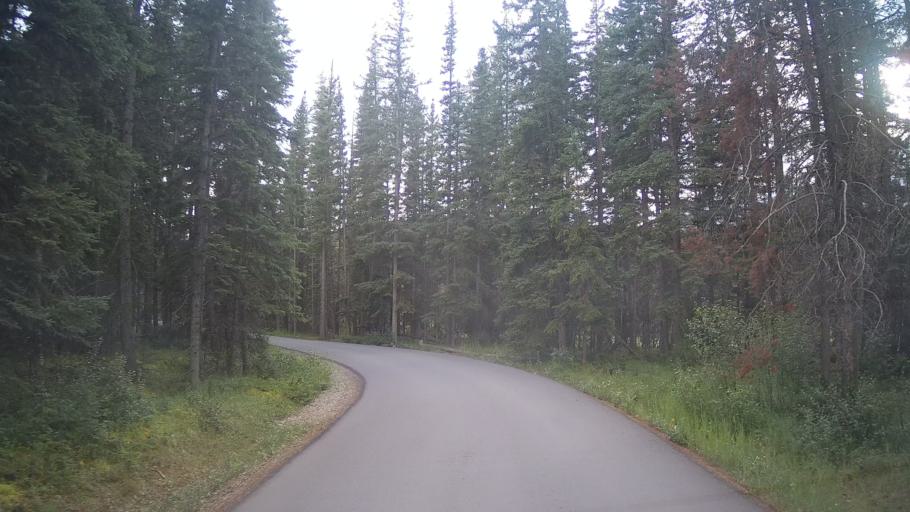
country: CA
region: Alberta
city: Jasper Park Lodge
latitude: 52.9331
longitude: -118.0320
